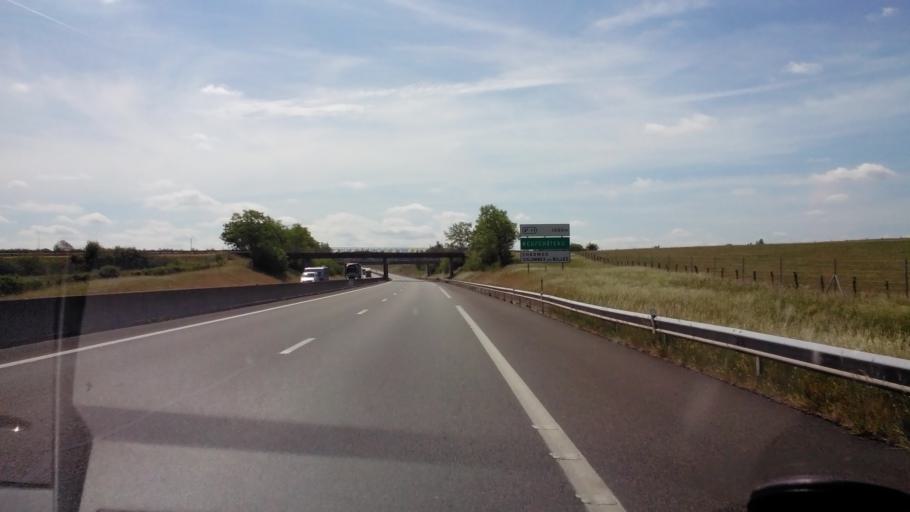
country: FR
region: Lorraine
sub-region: Departement de Meurthe-et-Moselle
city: Colombey-les-Belles
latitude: 48.5492
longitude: 5.8941
